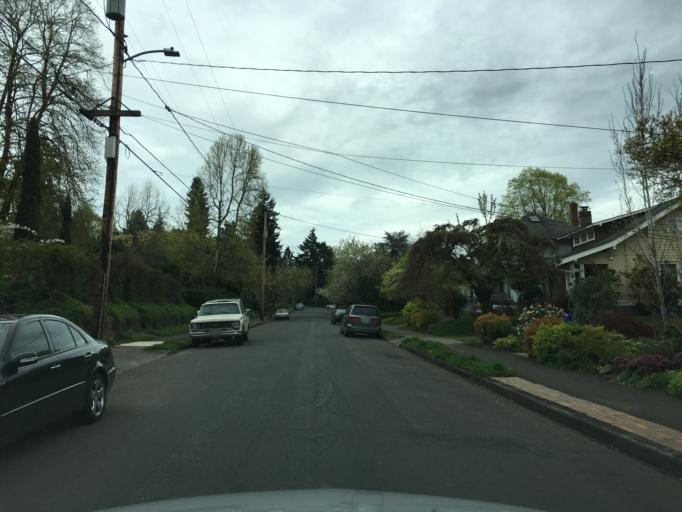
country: US
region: Oregon
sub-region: Multnomah County
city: Lents
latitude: 45.5211
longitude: -122.5996
